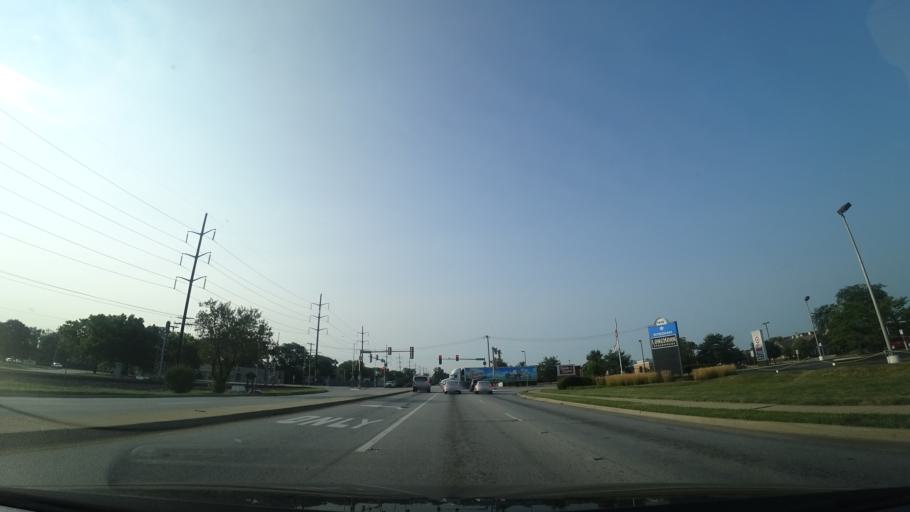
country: US
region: Illinois
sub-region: Cook County
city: Rosemont
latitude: 42.0103
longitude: -87.8862
